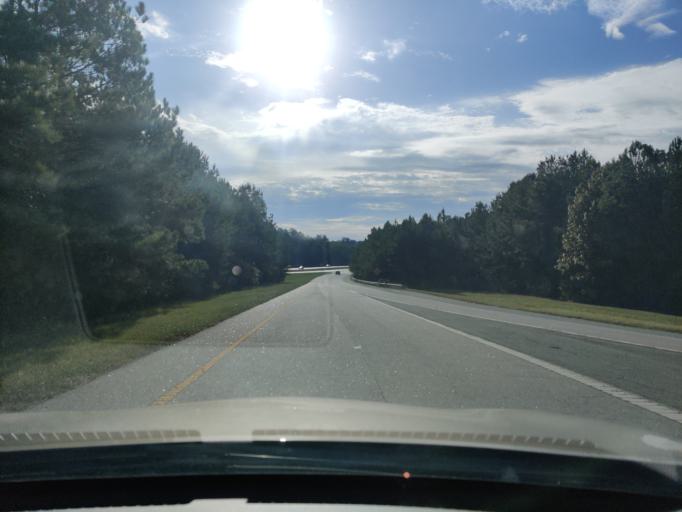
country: US
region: North Carolina
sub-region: Wake County
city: Morrisville
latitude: 35.8884
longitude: -78.8142
